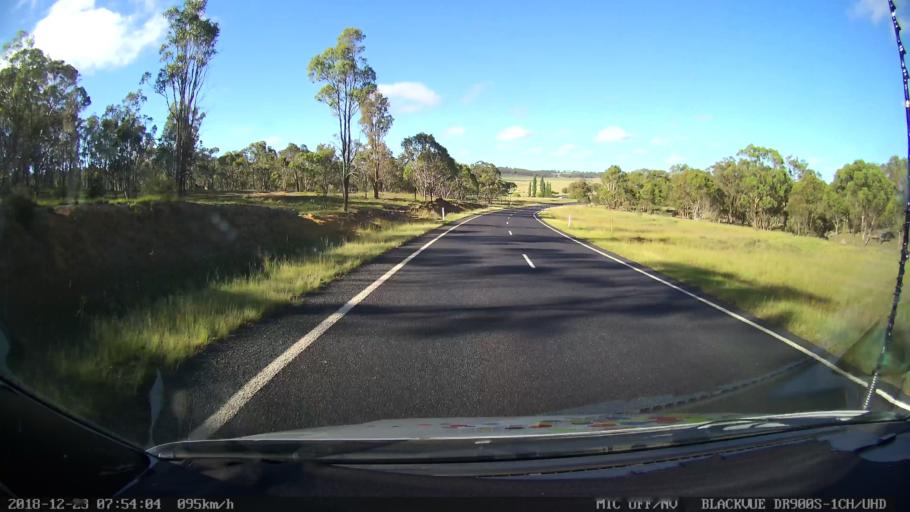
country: AU
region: New South Wales
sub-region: Armidale Dumaresq
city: Armidale
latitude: -30.5427
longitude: 151.8018
